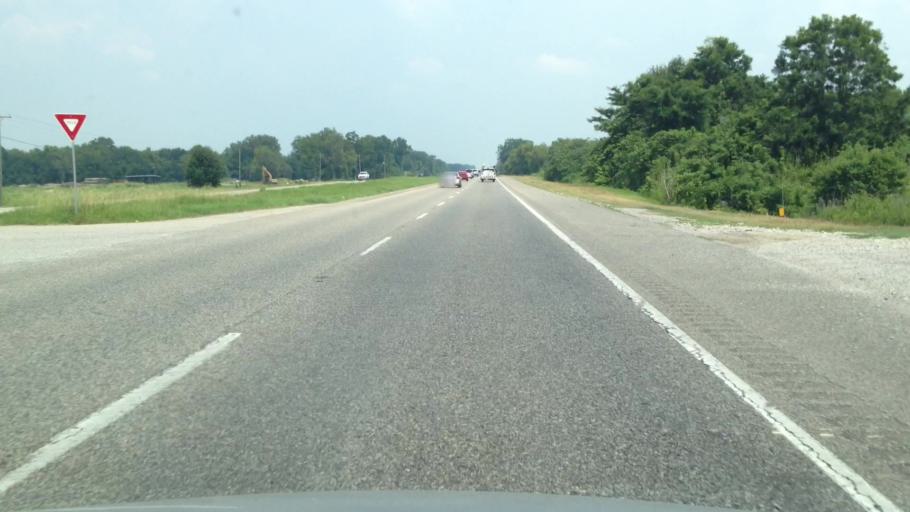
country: US
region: Louisiana
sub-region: West Baton Rouge Parish
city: Erwinville
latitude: 30.5147
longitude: -91.3531
